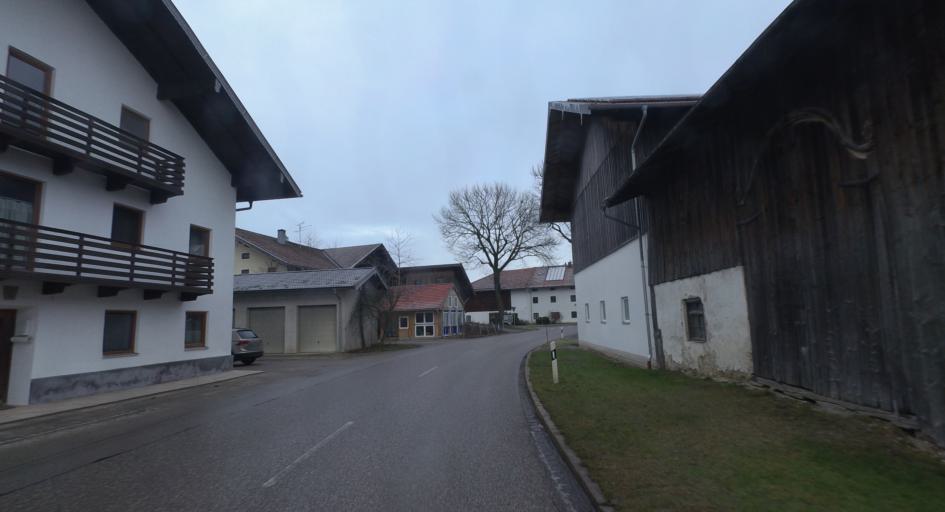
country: DE
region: Bavaria
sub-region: Upper Bavaria
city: Traunreut
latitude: 47.9405
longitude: 12.6459
